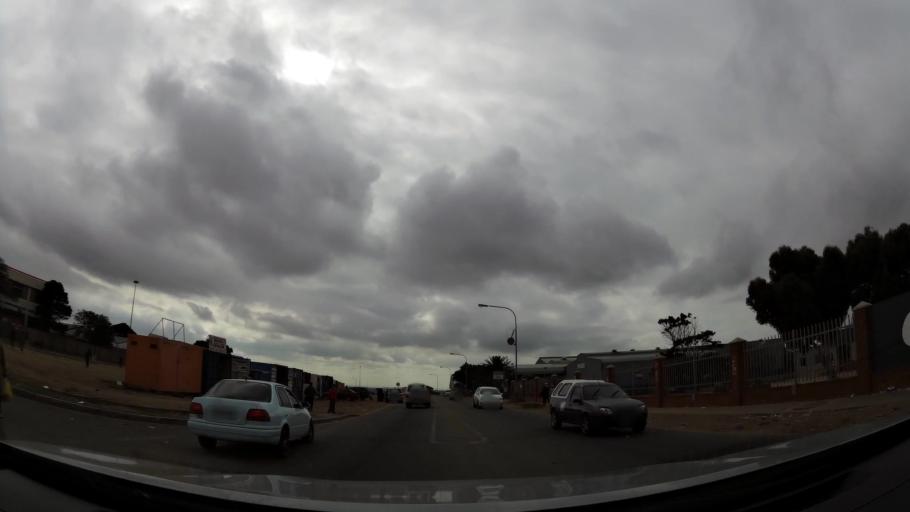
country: ZA
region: Eastern Cape
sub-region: Nelson Mandela Bay Metropolitan Municipality
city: Port Elizabeth
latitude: -33.8825
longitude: 25.5632
